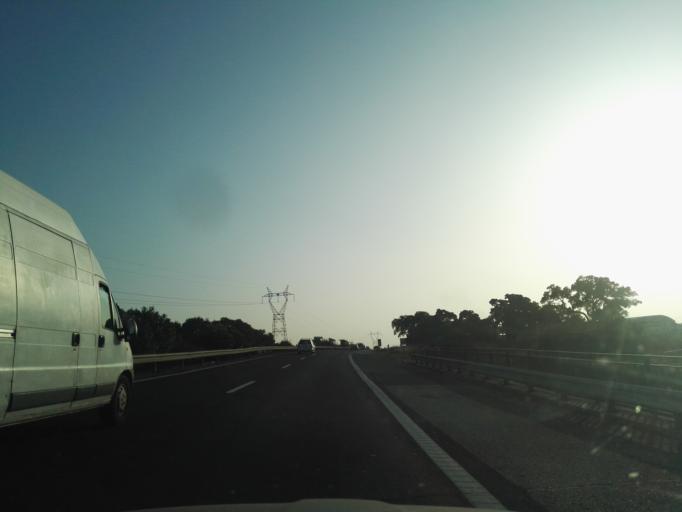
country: PT
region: Setubal
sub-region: Moita
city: Moita
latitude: 38.6523
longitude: -8.9673
